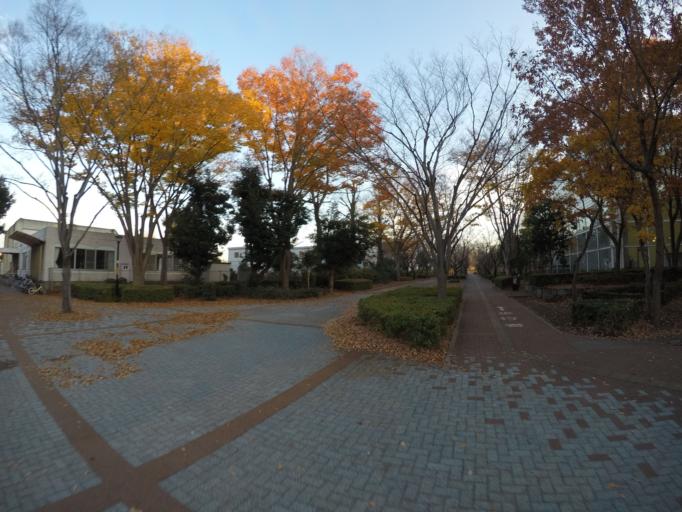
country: JP
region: Ibaraki
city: Naka
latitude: 36.0767
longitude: 140.1171
